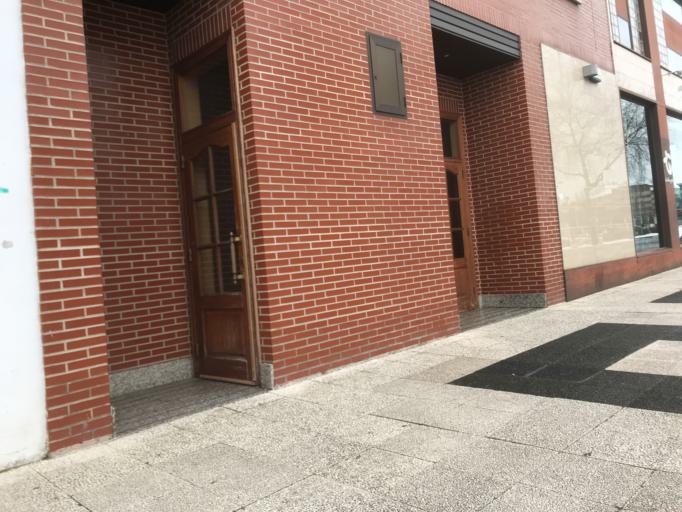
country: ES
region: Basque Country
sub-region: Provincia de Alava
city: Gasteiz / Vitoria
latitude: 42.8599
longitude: -2.6870
